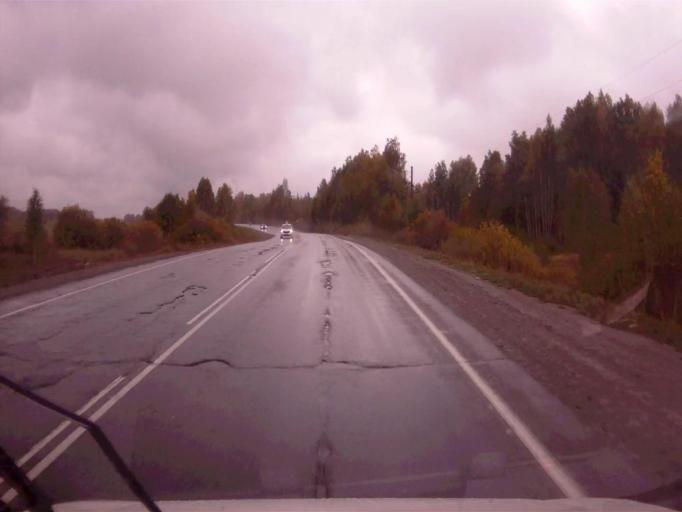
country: RU
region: Chelyabinsk
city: Argayash
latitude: 55.4858
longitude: 60.7385
